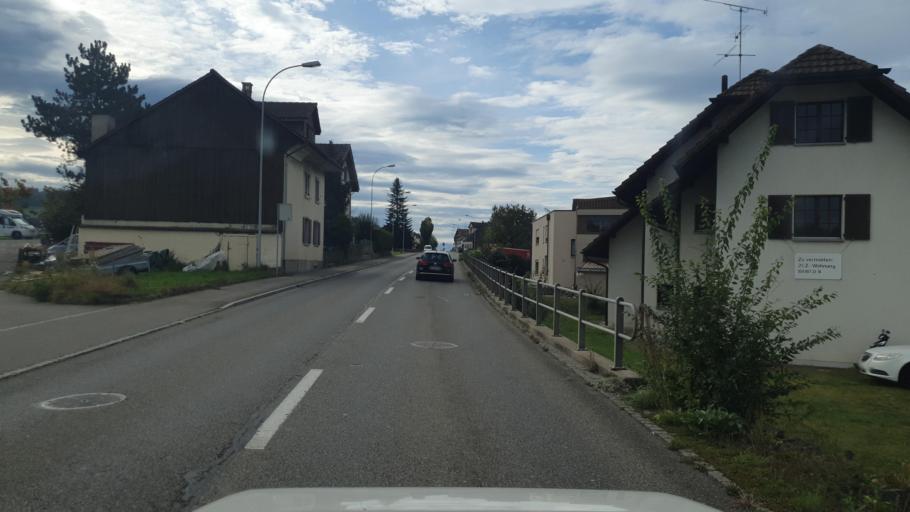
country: CH
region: Aargau
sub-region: Bezirk Bremgarten
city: Sarmenstorf
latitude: 47.3164
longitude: 8.2465
